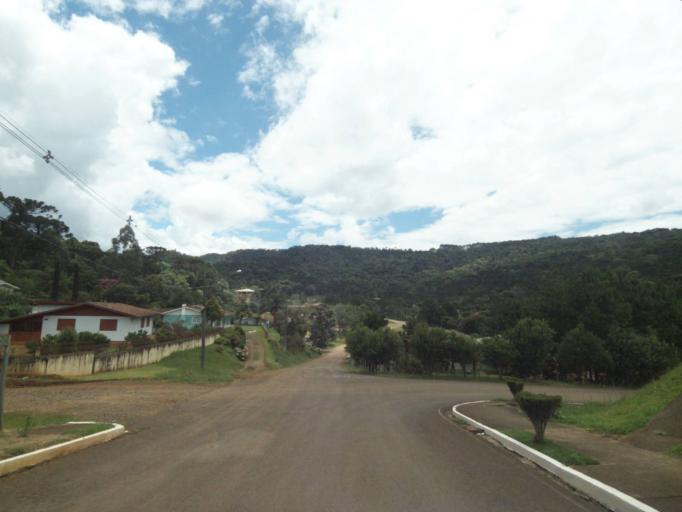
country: BR
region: Parana
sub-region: Pinhao
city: Pinhao
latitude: -26.1577
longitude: -51.5623
